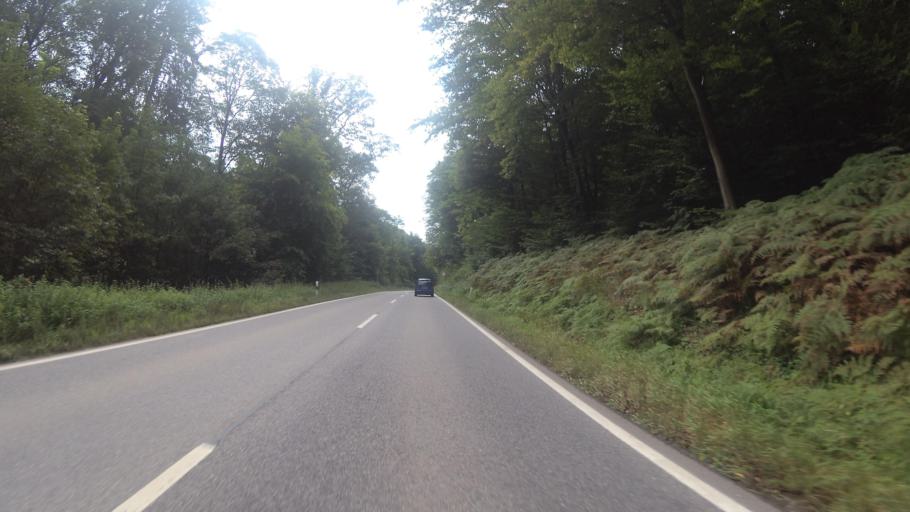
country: DE
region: Saarland
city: Grossrosseln
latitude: 49.2127
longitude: 6.8221
